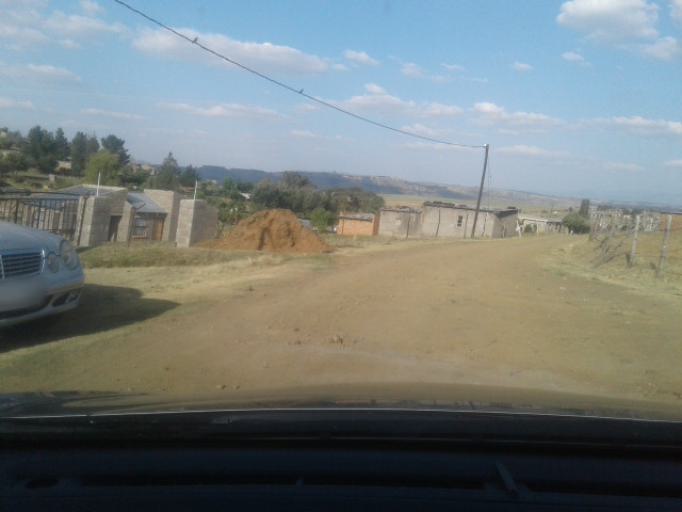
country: LS
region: Berea
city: Teyateyaneng
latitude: -29.1541
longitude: 27.7568
